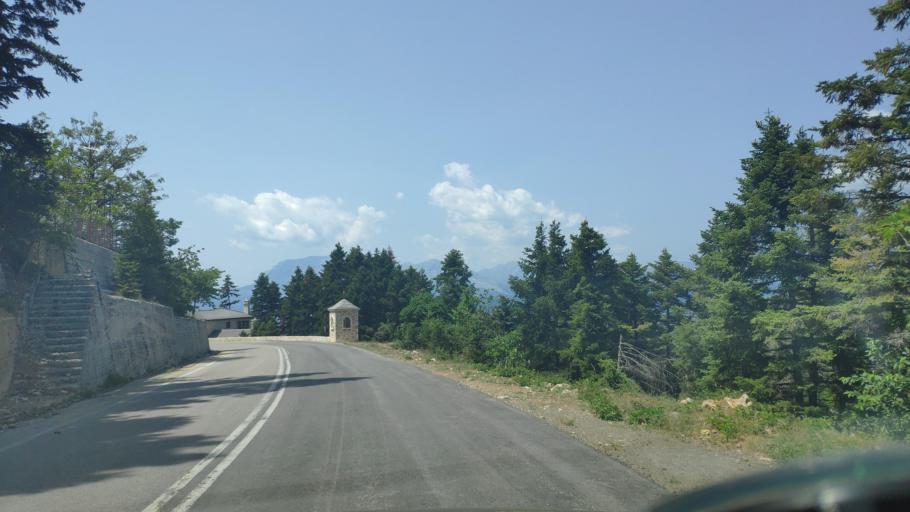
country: GR
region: Epirus
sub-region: Nomos Artas
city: Ano Kalentini
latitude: 39.2683
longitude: 21.2584
